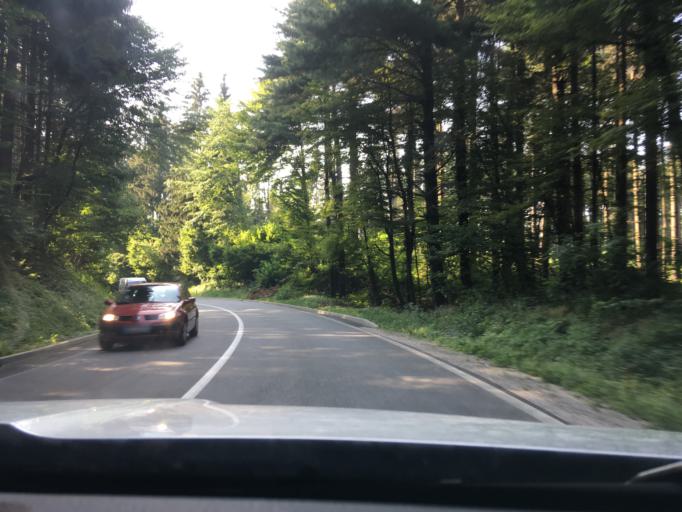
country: SI
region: Semic
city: Semic
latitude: 45.7273
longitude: 15.2338
